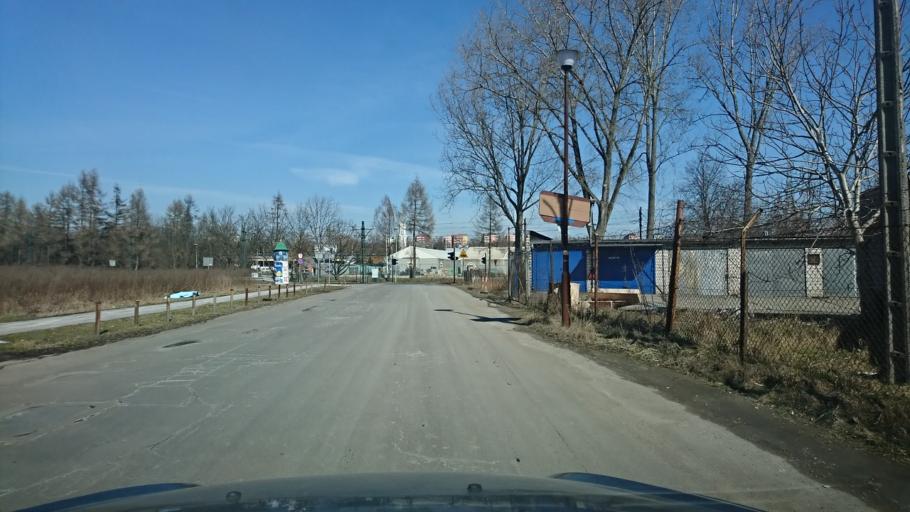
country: PL
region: Lesser Poland Voivodeship
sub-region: Powiat wielicki
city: Kokotow
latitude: 50.0874
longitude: 20.0597
